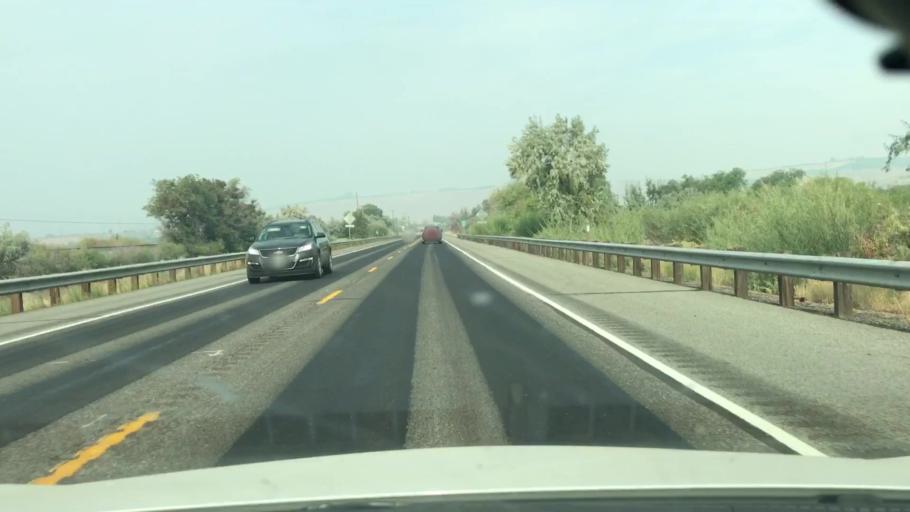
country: US
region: Washington
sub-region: Chelan County
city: South Wenatchee
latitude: 47.3661
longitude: -120.1219
